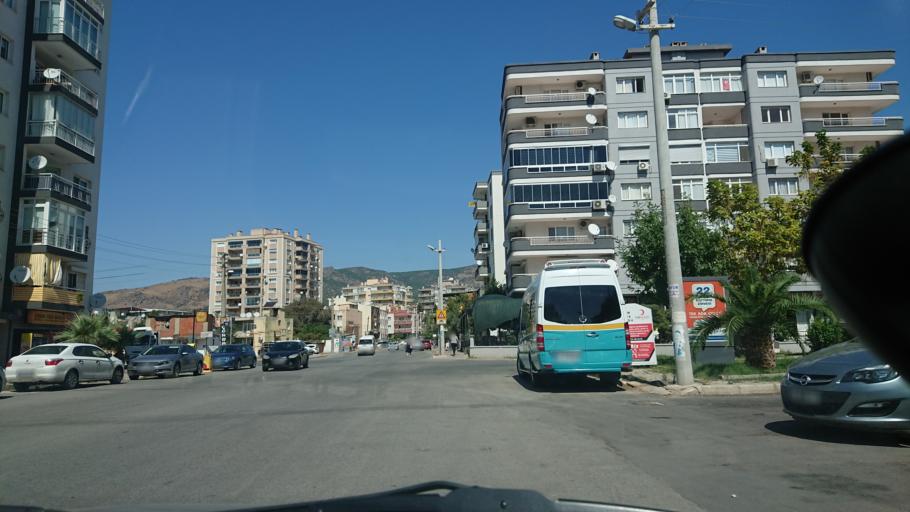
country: TR
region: Izmir
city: Karsiyaka
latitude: 38.4796
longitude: 27.1176
